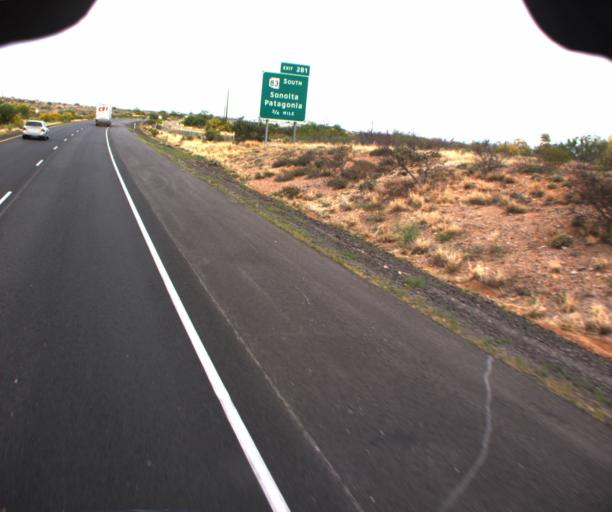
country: US
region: Arizona
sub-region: Pima County
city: Vail
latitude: 32.0016
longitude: -110.6790
